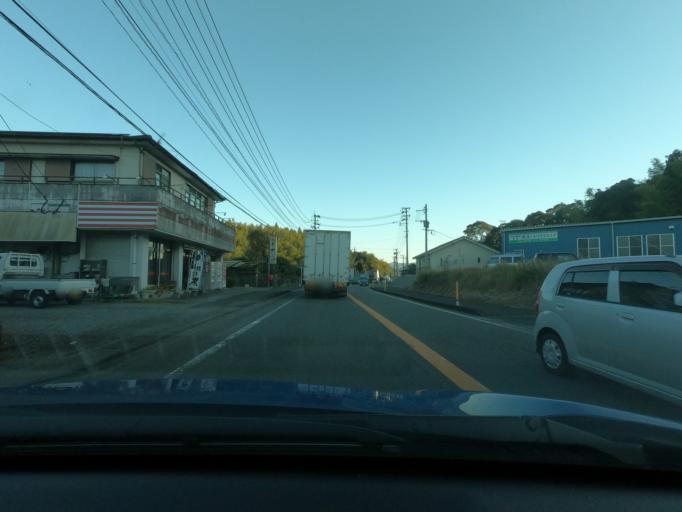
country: JP
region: Kagoshima
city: Satsumasendai
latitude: 31.8414
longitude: 130.2818
